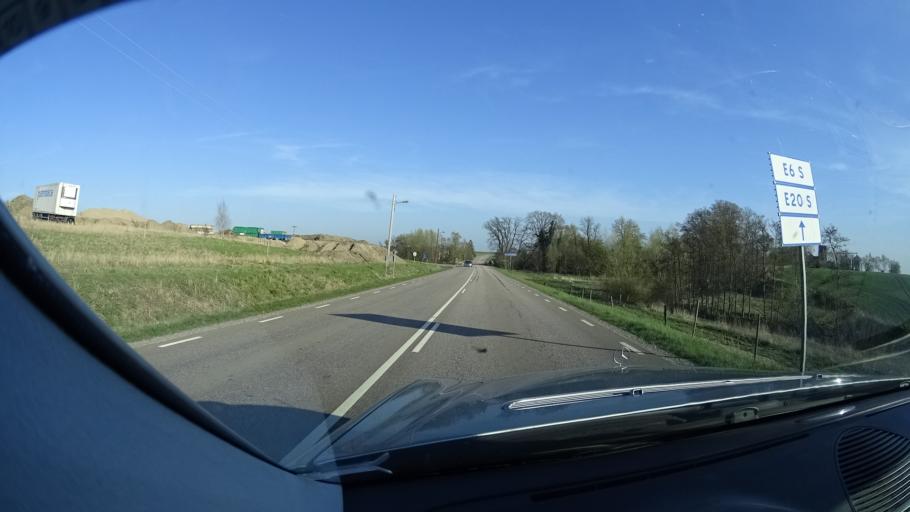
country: SE
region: Skane
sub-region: Landskrona
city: Asmundtorp
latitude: 55.8854
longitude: 12.9693
